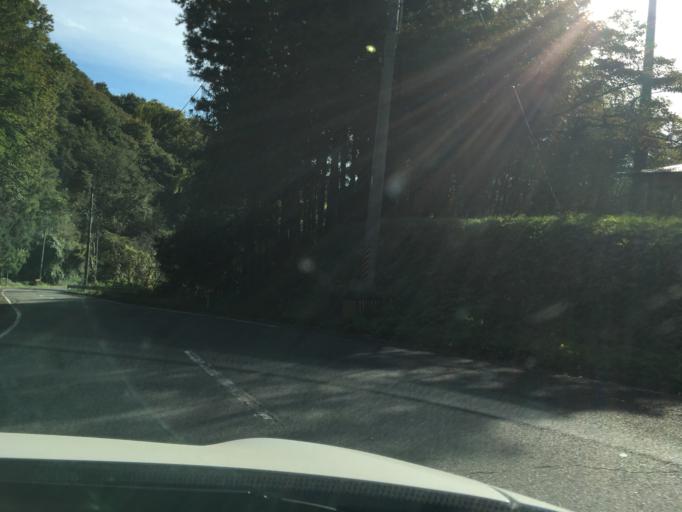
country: JP
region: Fukushima
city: Ishikawa
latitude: 37.1743
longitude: 140.4706
